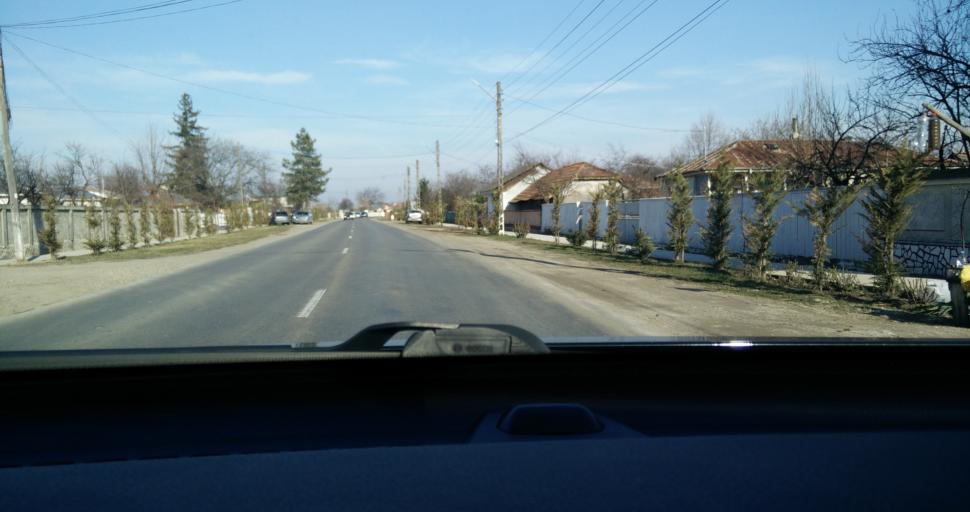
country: RO
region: Vrancea
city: Vulturu de Sus
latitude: 45.6201
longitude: 27.4171
